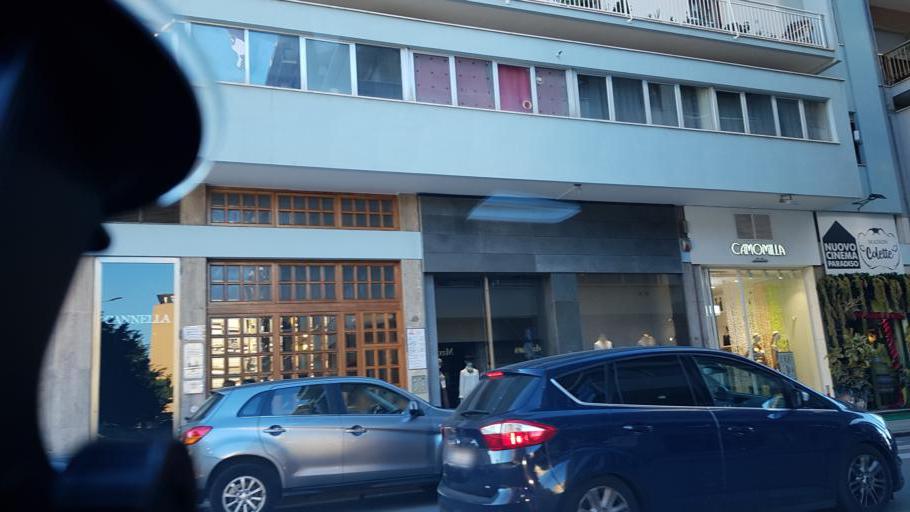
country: IT
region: Apulia
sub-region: Provincia di Lecce
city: Lecce
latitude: 40.3540
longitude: 18.1800
